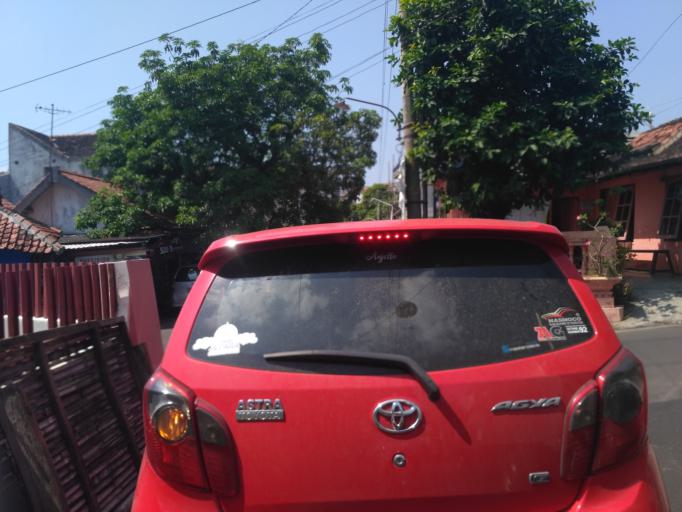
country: ID
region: Central Java
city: Semarang
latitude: -7.0051
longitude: 110.4243
